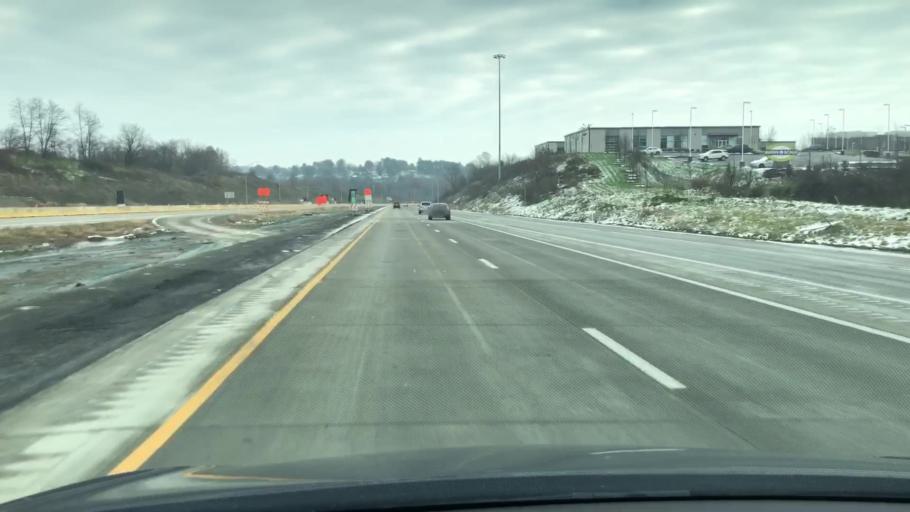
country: US
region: Pennsylvania
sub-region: Allegheny County
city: Enlow
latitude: 40.4721
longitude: -80.2204
